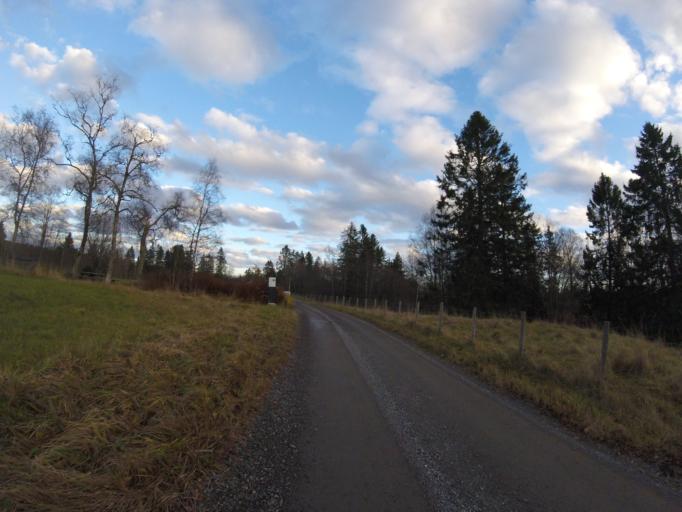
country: NO
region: Akershus
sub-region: Skedsmo
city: Leirsund
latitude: 60.0003
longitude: 11.0543
